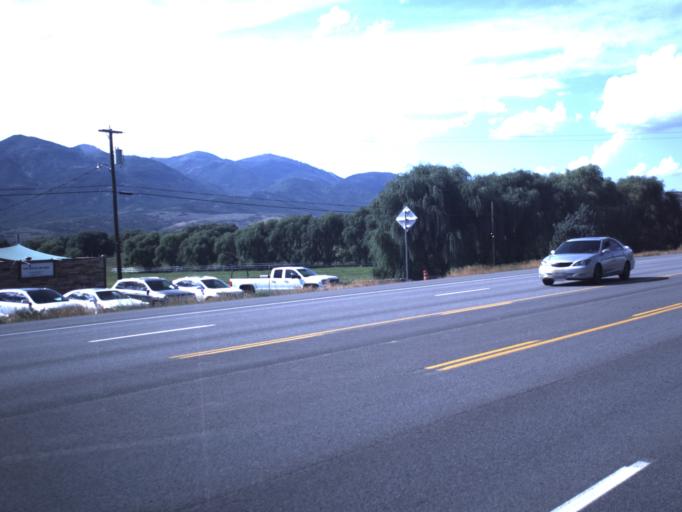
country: US
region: Utah
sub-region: Wasatch County
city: Heber
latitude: 40.5214
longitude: -111.4108
